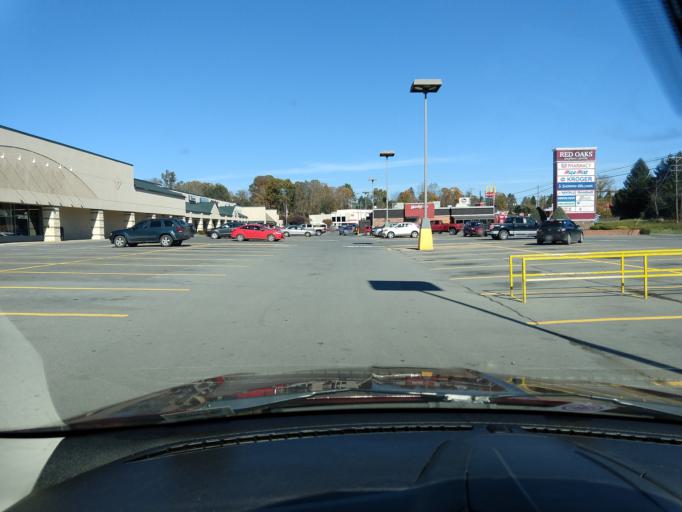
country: US
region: West Virginia
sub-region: Greenbrier County
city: Fairlea
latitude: 37.7667
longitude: -80.4668
